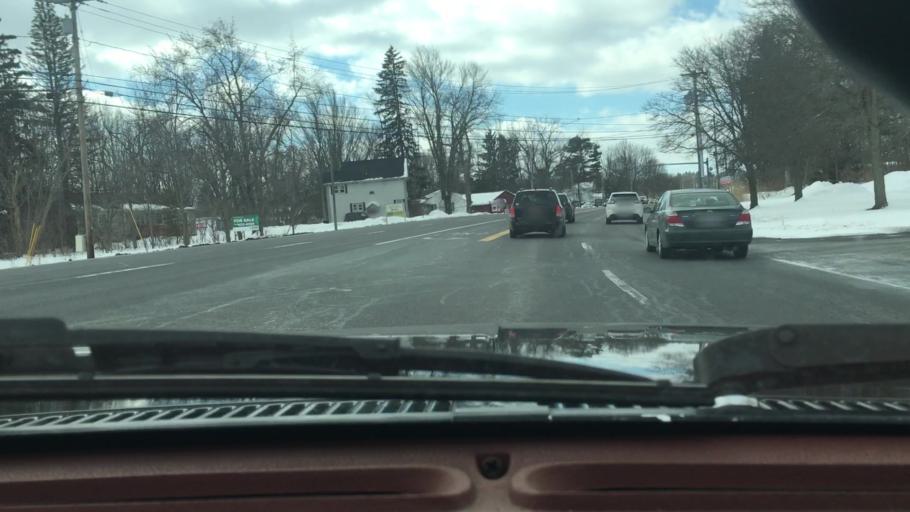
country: US
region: New York
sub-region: Onondaga County
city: Liverpool
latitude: 43.1551
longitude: -76.2274
